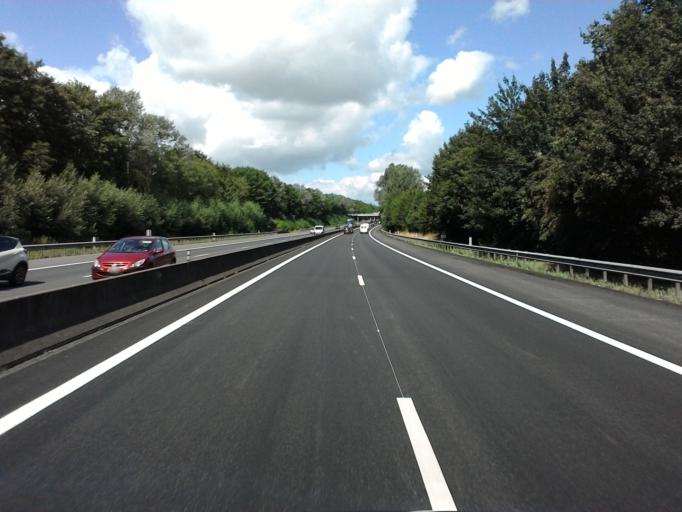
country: LU
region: Luxembourg
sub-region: Canton de Capellen
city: Mamer
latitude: 49.6323
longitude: 6.0371
